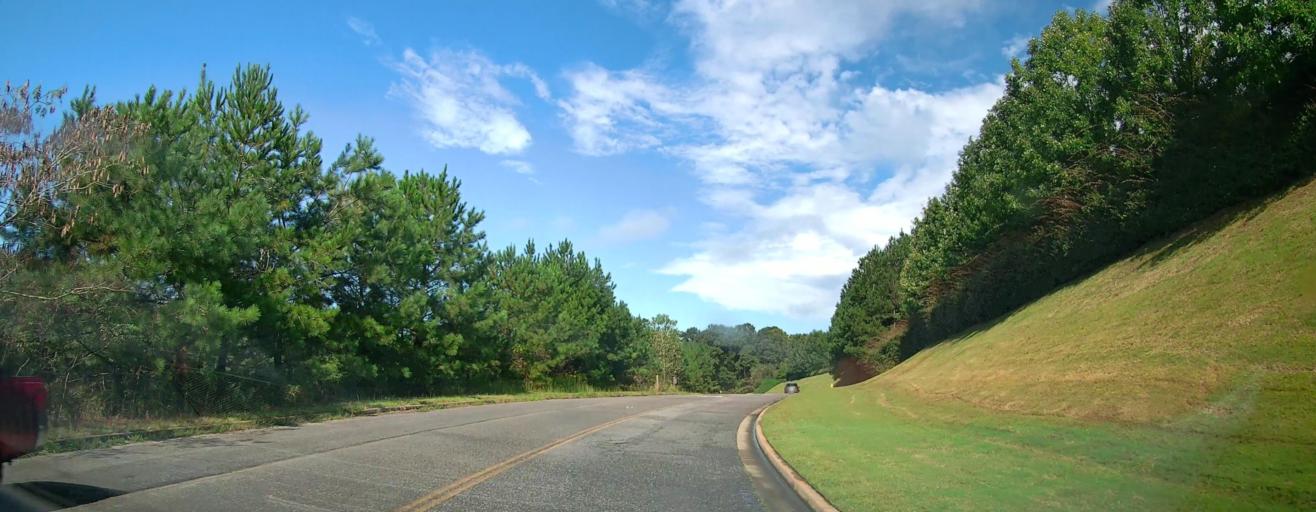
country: US
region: Georgia
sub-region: Bibb County
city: Macon
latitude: 32.9235
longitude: -83.7154
